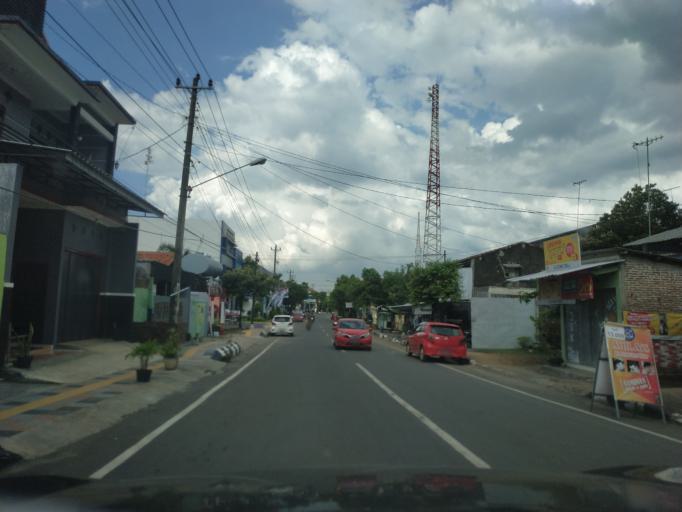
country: ID
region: Central Java
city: Pati
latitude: -6.7548
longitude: 111.0345
